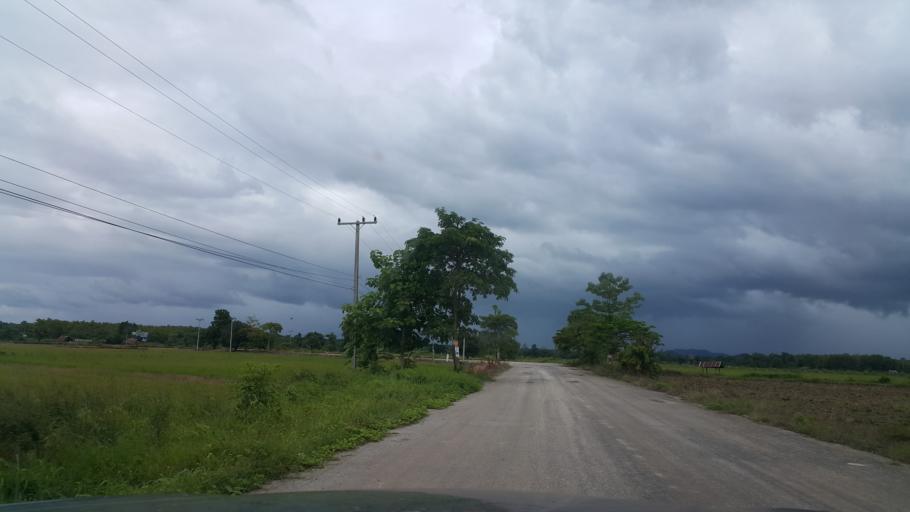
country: TH
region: Sukhothai
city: Thung Saliam
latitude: 17.3126
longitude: 99.5777
